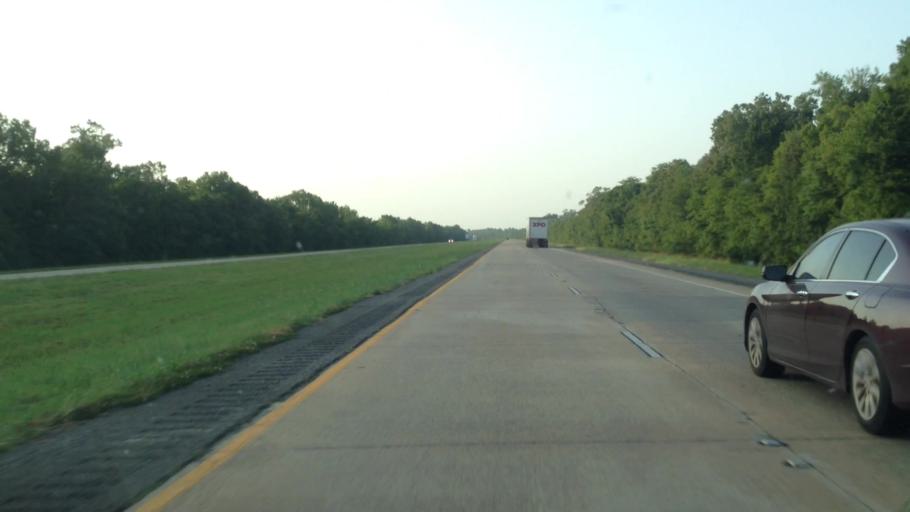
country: US
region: Louisiana
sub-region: Natchitoches Parish
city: Vienna Bend
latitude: 31.5872
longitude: -93.0298
